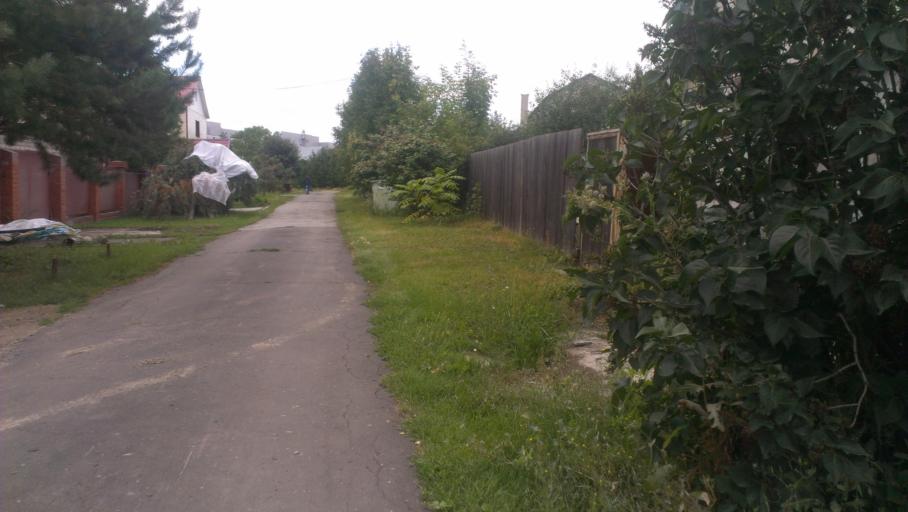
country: RU
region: Altai Krai
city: Novosilikatnyy
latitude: 53.3498
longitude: 83.6426
